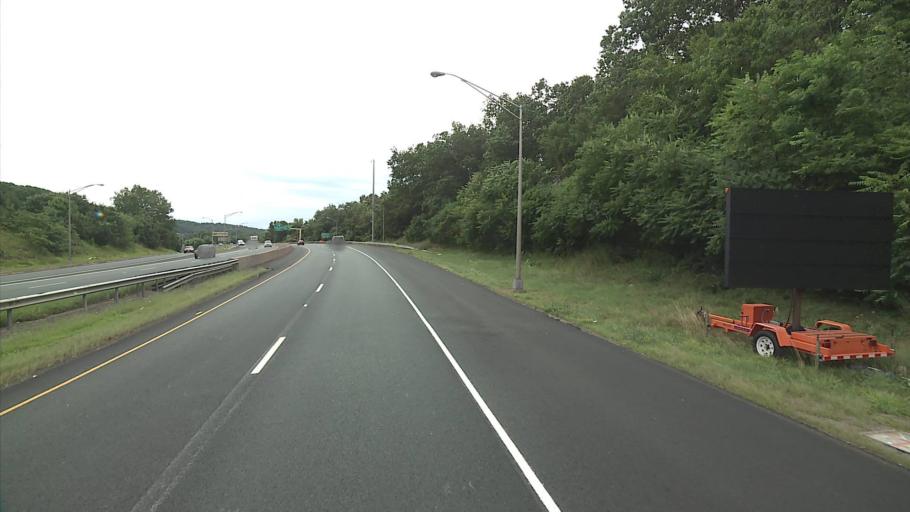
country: US
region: Connecticut
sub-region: New Haven County
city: Naugatuck
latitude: 41.5169
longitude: -73.0496
